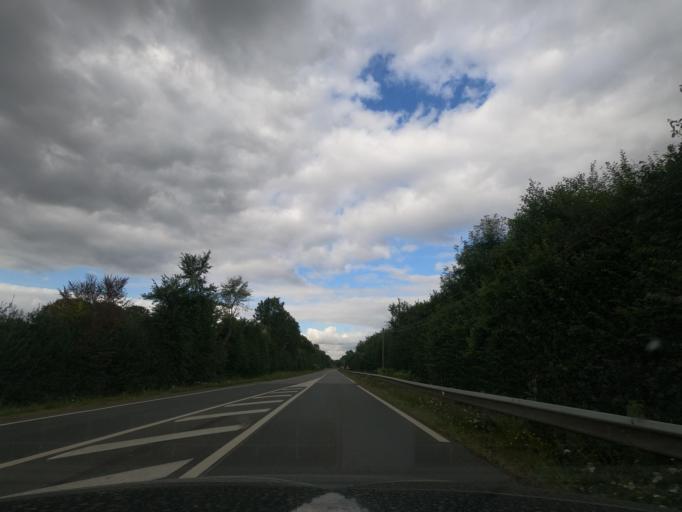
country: FR
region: Lower Normandy
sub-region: Departement de l'Orne
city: Gace
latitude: 48.8682
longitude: 0.3750
